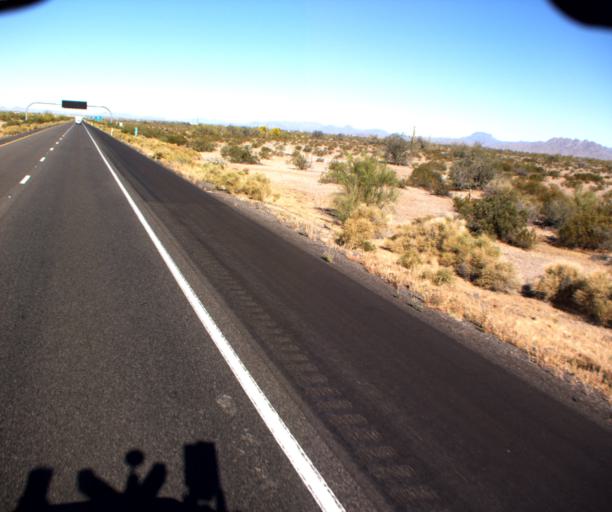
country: US
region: Arizona
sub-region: Maricopa County
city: Gila Bend
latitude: 32.9195
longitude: -112.6440
